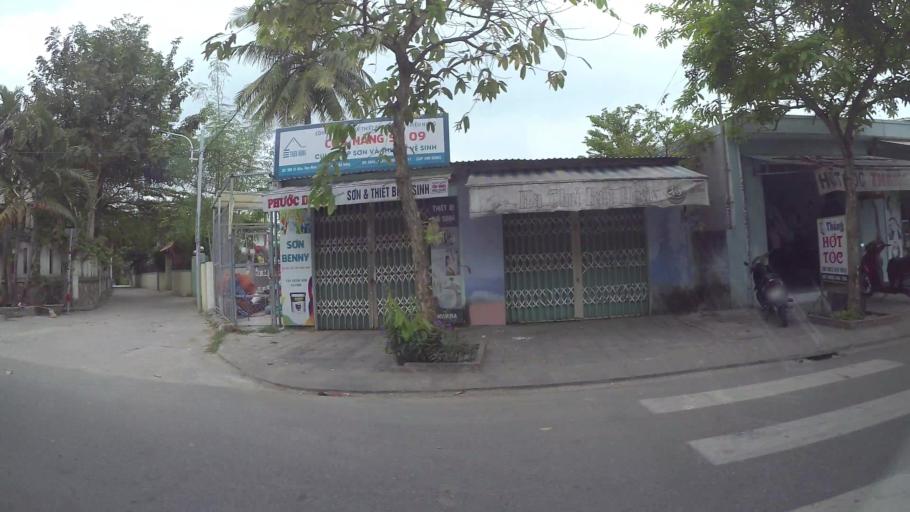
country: VN
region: Da Nang
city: Lien Chieu
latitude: 16.0583
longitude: 108.1683
